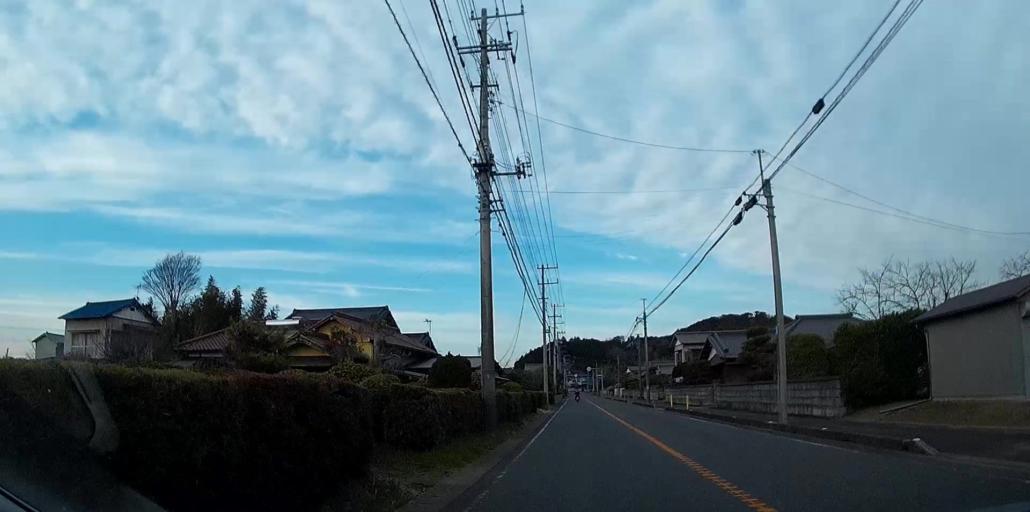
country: JP
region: Chiba
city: Kisarazu
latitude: 35.3741
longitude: 140.0615
